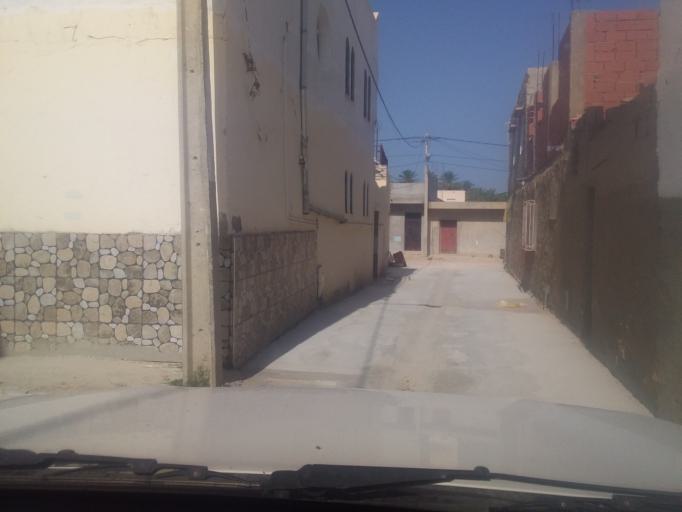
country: TN
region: Qabis
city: Gabes
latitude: 33.6229
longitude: 10.2858
